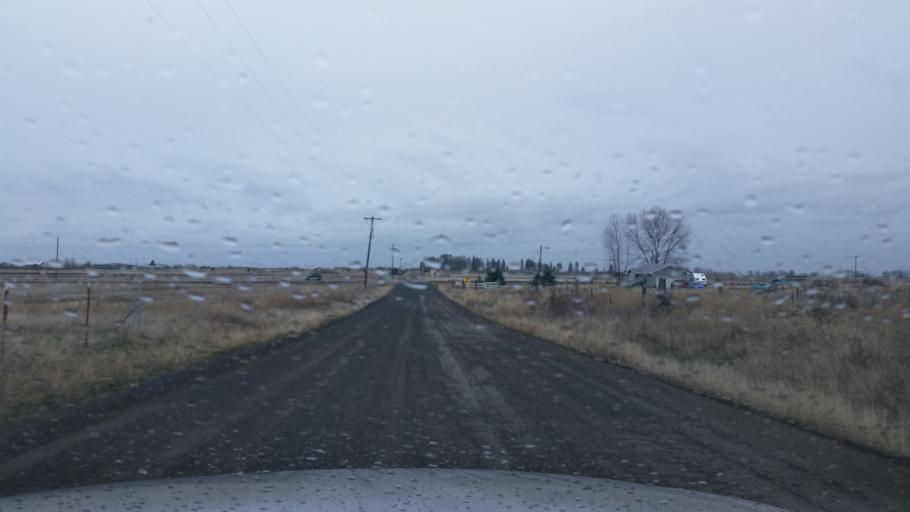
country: US
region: Washington
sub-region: Spokane County
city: Fairchild Air Force Base
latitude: 47.5890
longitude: -117.6289
